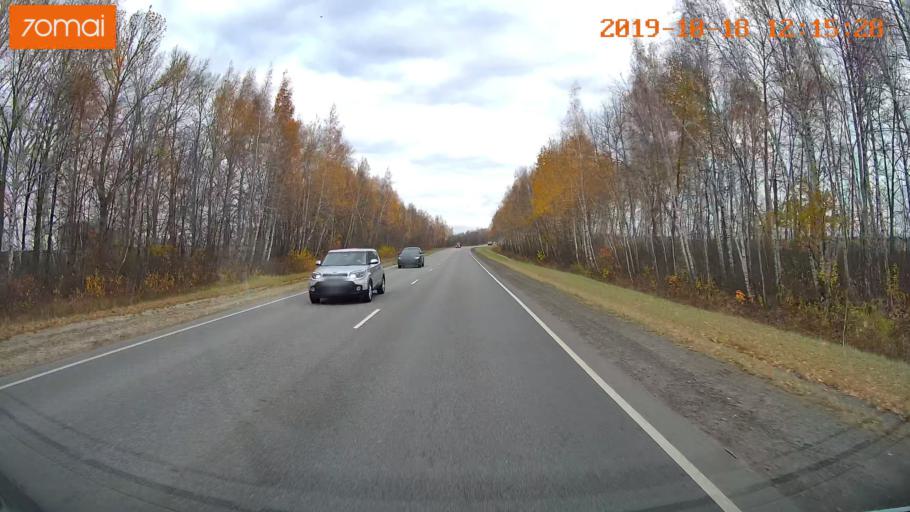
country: RU
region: Rjazan
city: Zakharovo
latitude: 54.4436
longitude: 39.3999
